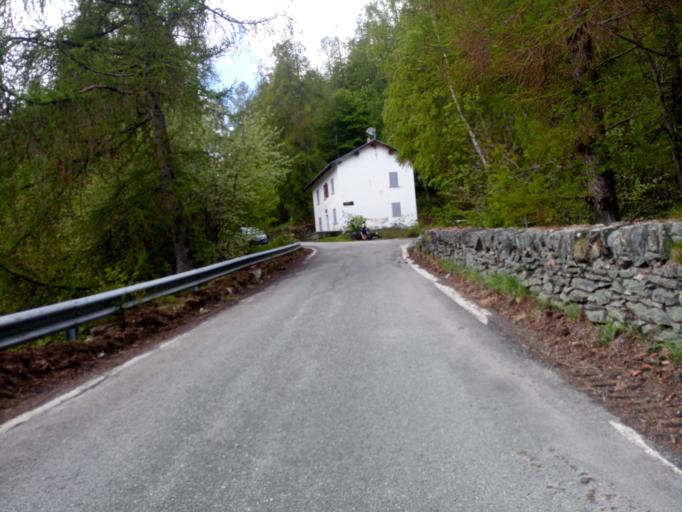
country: IT
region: Piedmont
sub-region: Provincia di Torino
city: Meana di Susa
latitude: 45.1008
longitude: 7.0637
